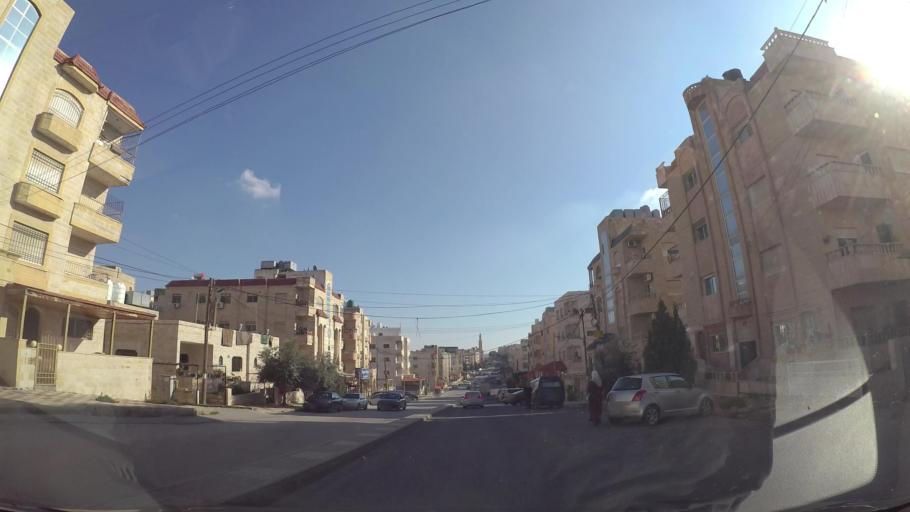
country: JO
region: Amman
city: Amman
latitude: 31.9844
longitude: 35.9461
